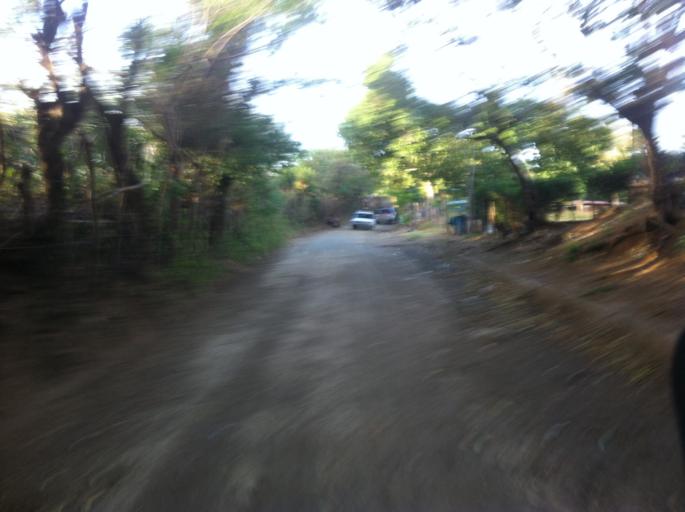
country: NI
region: Managua
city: Managua
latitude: 12.0812
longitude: -86.3107
